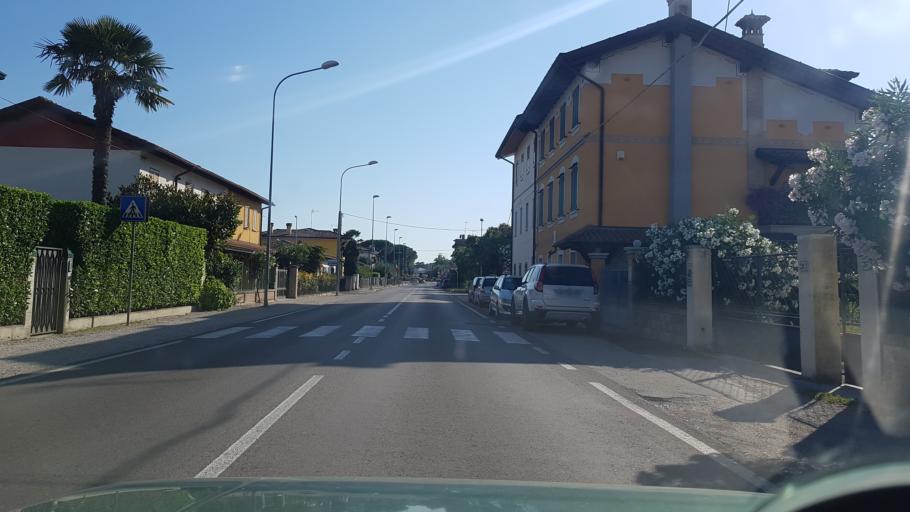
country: IT
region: Friuli Venezia Giulia
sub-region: Provincia di Udine
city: Cervignano del Friuli
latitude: 45.8277
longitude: 13.3436
